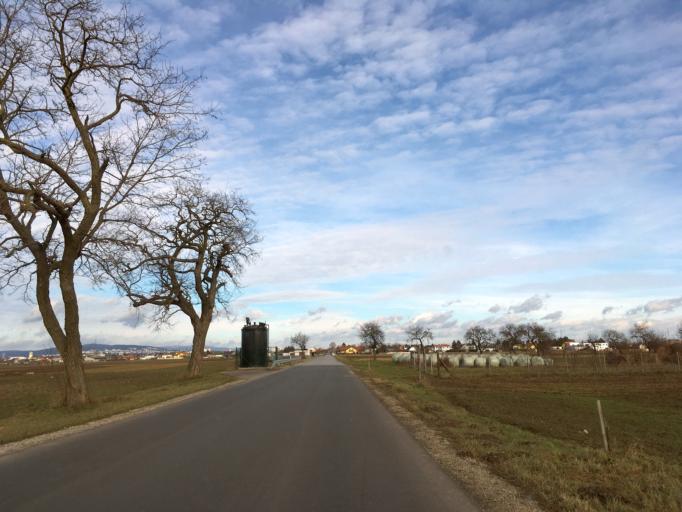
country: AT
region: Burgenland
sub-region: Politischer Bezirk Neusiedl am See
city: Kittsee
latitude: 48.0772
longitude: 17.0619
